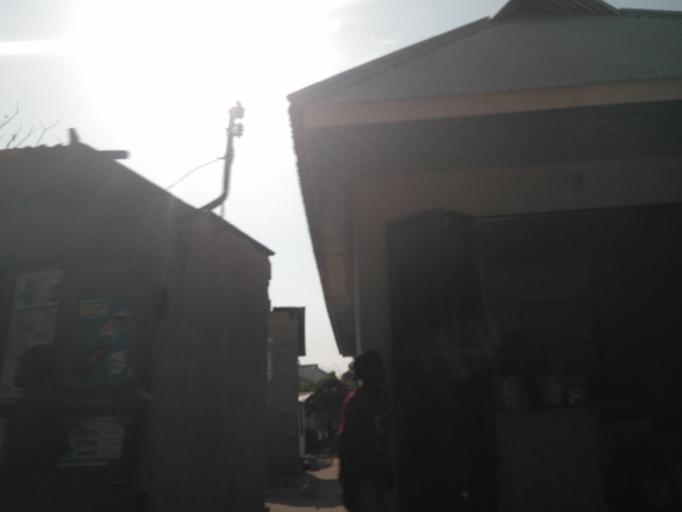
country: TZ
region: Dar es Salaam
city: Dar es Salaam
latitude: -6.8660
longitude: 39.3109
